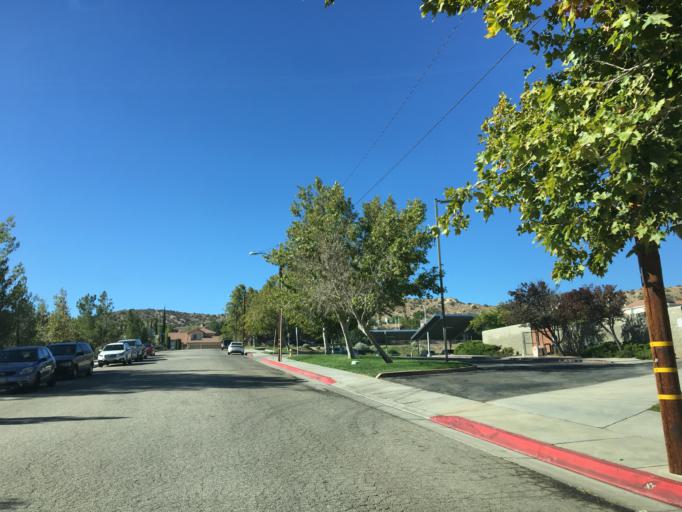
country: US
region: California
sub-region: Los Angeles County
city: Desert View Highlands
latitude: 34.5856
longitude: -118.1540
